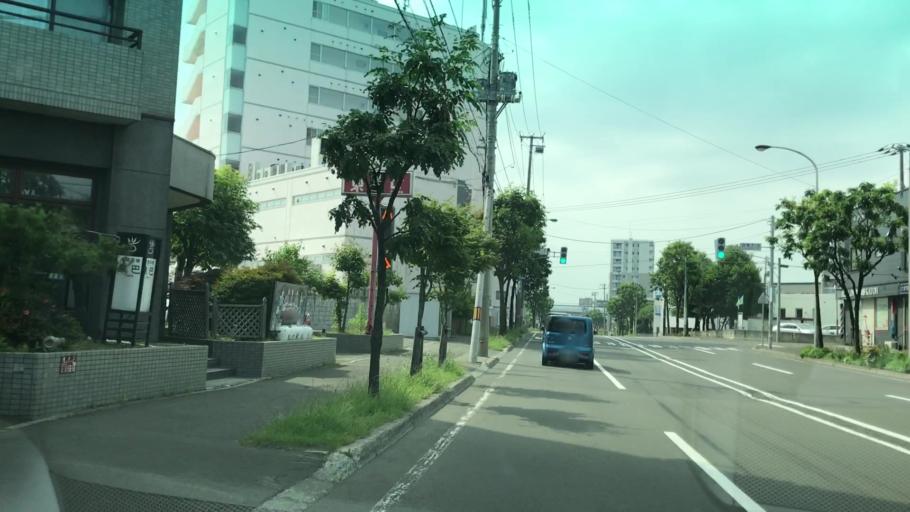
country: JP
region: Hokkaido
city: Sapporo
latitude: 43.0908
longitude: 141.2882
